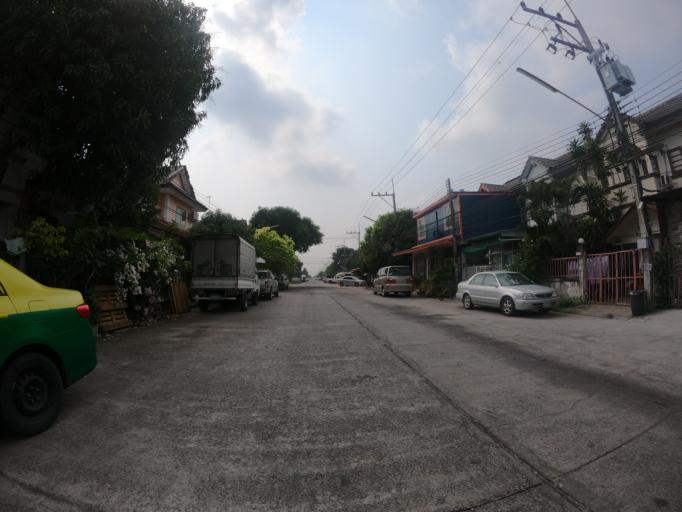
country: TH
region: Pathum Thani
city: Nong Suea
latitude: 14.0754
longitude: 100.8585
